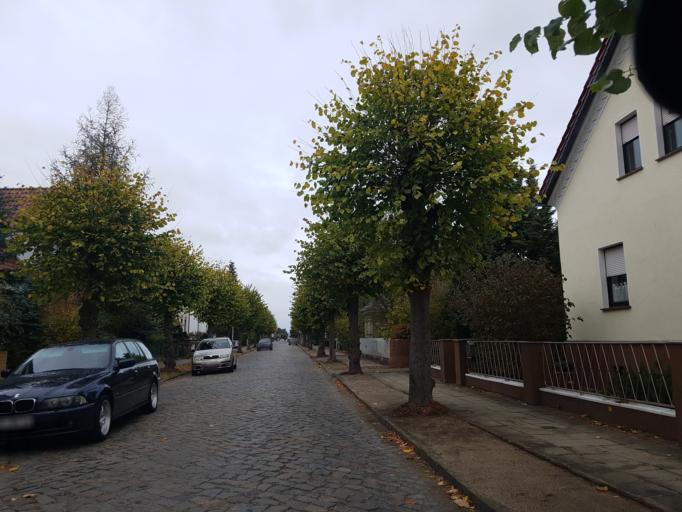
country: DE
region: Brandenburg
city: Herzberg
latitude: 51.6884
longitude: 13.2287
